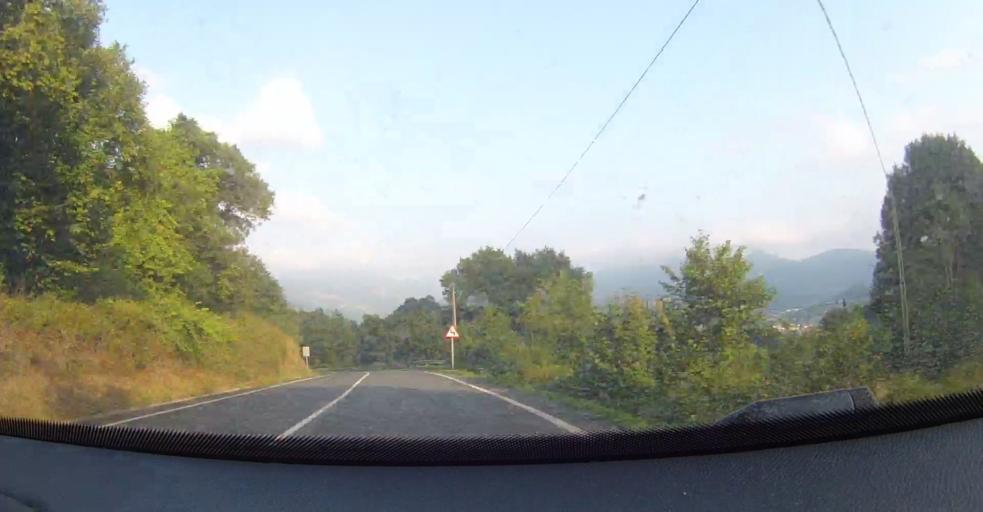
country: ES
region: Basque Country
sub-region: Bizkaia
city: Sopuerta
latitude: 43.2898
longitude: -3.1635
